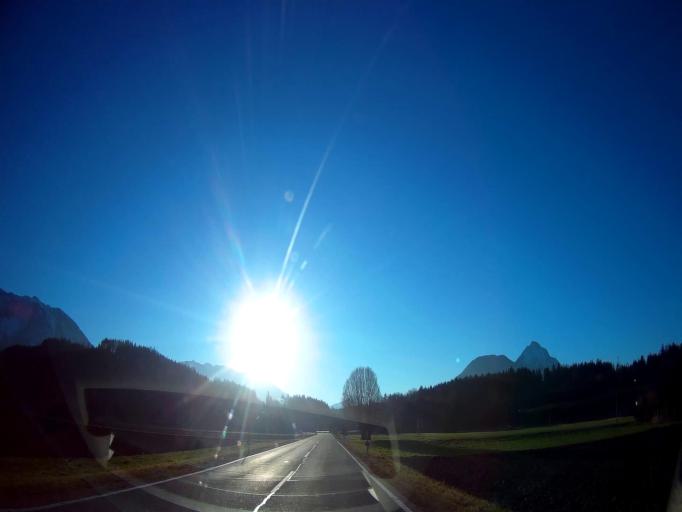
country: DE
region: Bavaria
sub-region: Upper Bavaria
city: Piding
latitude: 47.7713
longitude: 12.9577
